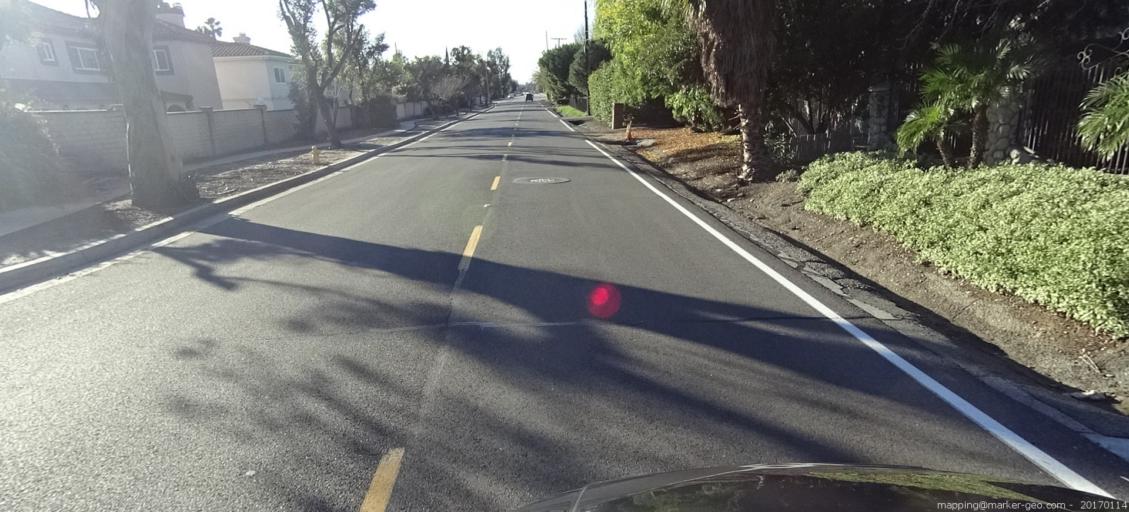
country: US
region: California
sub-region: Orange County
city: North Tustin
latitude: 33.7735
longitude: -117.8028
